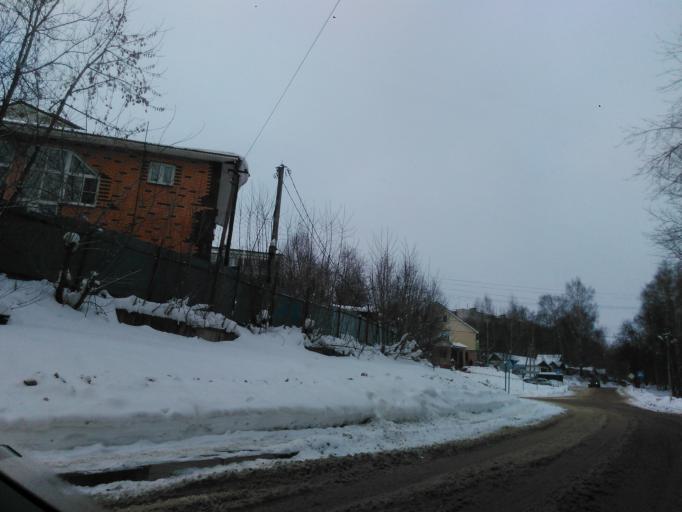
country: RU
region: Moskovskaya
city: Yakhroma
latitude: 56.2816
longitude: 37.4859
